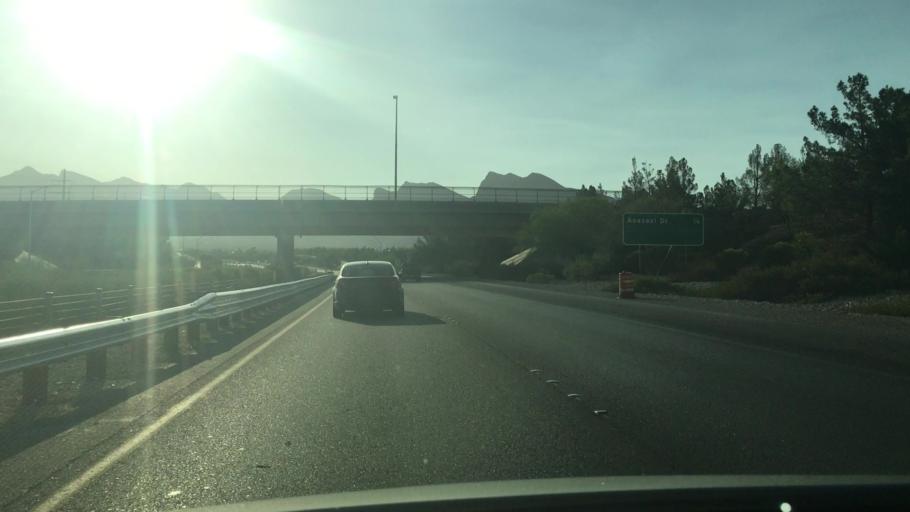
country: US
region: Nevada
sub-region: Clark County
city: Summerlin South
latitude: 36.1918
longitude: -115.3149
